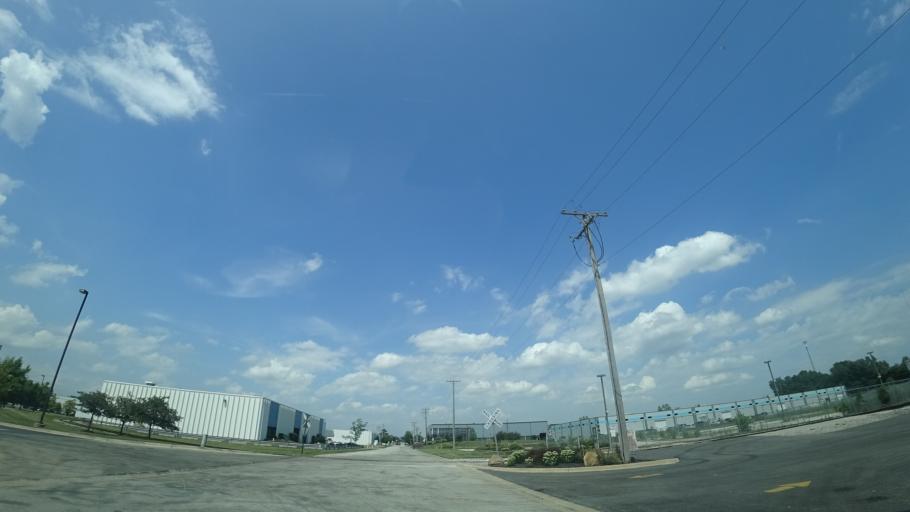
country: US
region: Illinois
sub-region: Cook County
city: Crestwood
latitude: 41.6756
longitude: -87.7684
